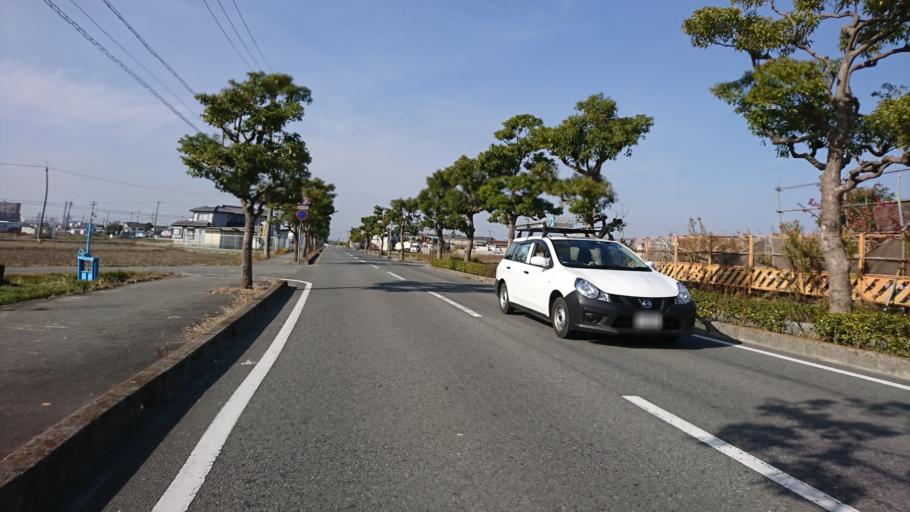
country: JP
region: Hyogo
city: Kakogawacho-honmachi
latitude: 34.7280
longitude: 134.8739
